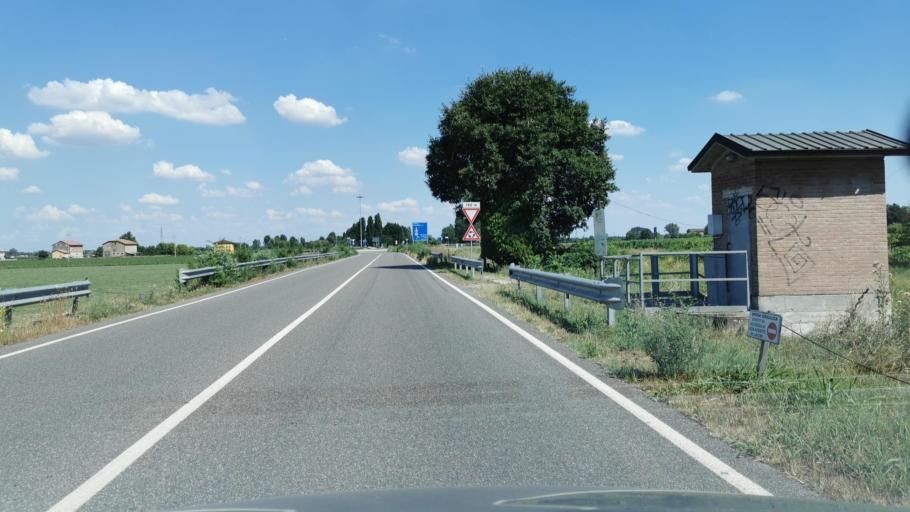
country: IT
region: Emilia-Romagna
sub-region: Provincia di Modena
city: Sam Marino
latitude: 44.7984
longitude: 10.9126
